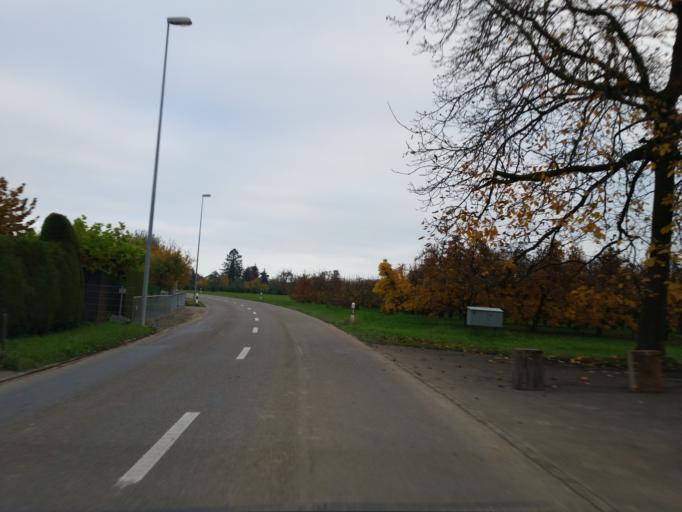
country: CH
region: Thurgau
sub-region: Arbon District
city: Salmsach
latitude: 47.5486
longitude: 9.3519
